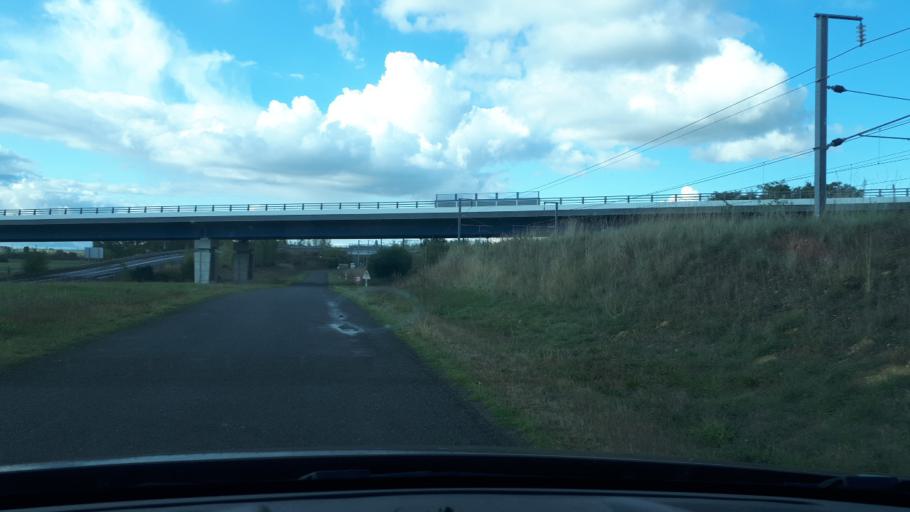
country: FR
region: Centre
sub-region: Departement du Loir-et-Cher
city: Mareuil-sur-Cher
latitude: 47.3034
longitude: 1.3499
